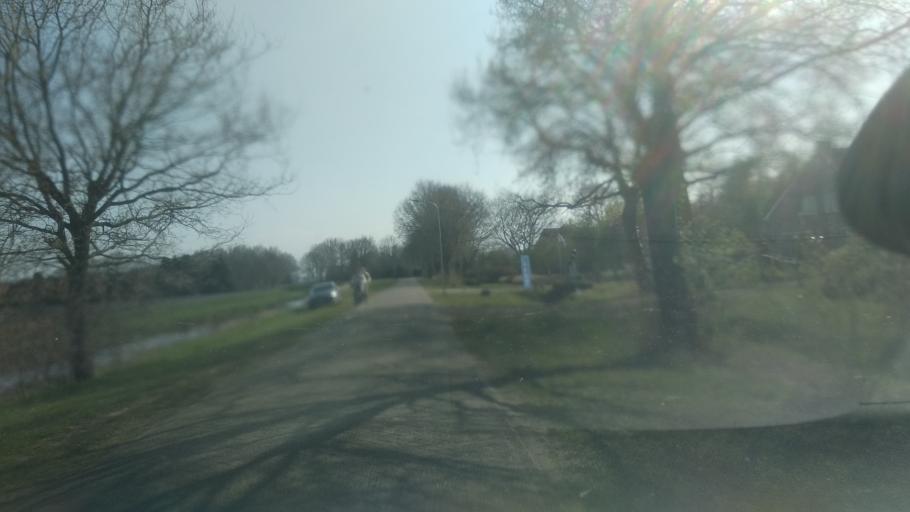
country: NL
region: Drenthe
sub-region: Gemeente Borger-Odoorn
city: Borger
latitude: 52.8741
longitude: 6.7607
